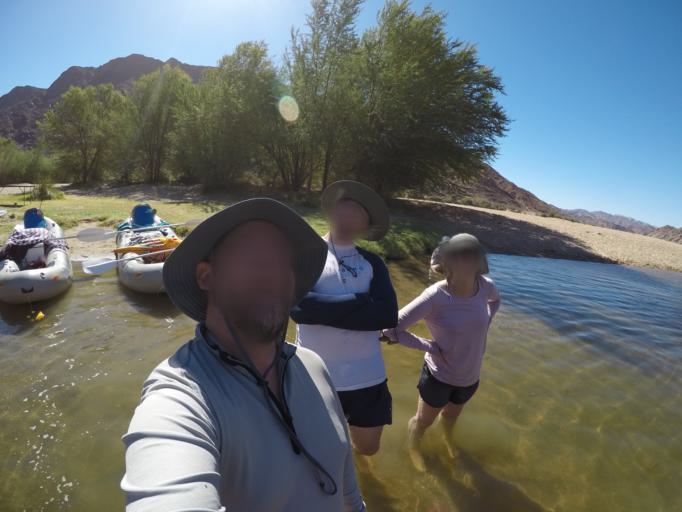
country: ZA
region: Northern Cape
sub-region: Namakwa District Municipality
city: Port Nolloth
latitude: -28.6218
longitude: 17.4292
